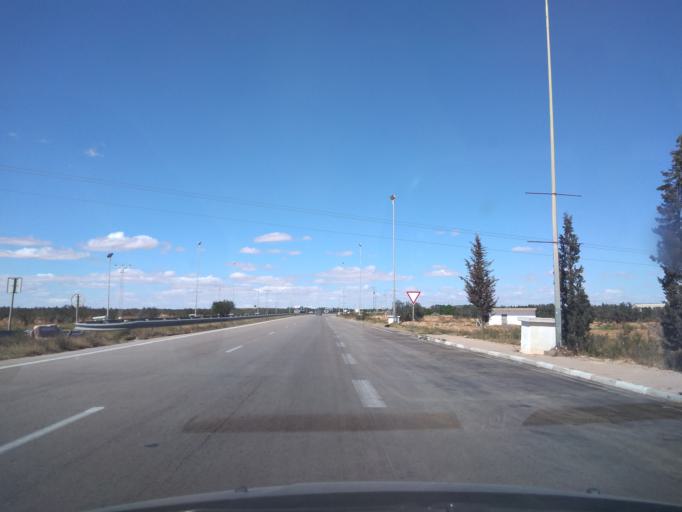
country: TN
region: Safaqis
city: Al Qarmadah
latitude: 34.8858
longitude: 10.7224
